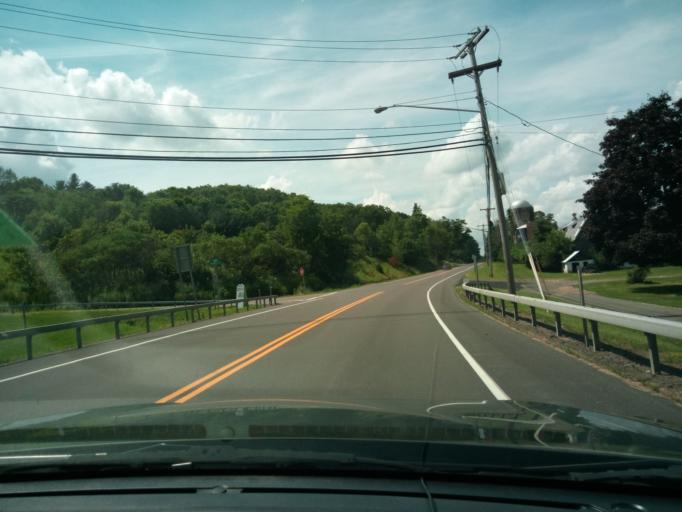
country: US
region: New York
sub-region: Chemung County
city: Southport
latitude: 42.0174
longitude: -76.7321
